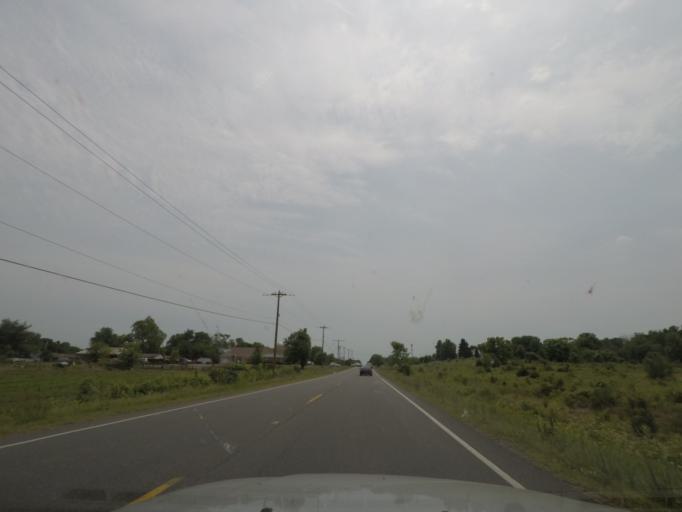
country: US
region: Virginia
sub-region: Prince William County
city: Bull Run Mountain Estates
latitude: 38.8879
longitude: -77.6325
